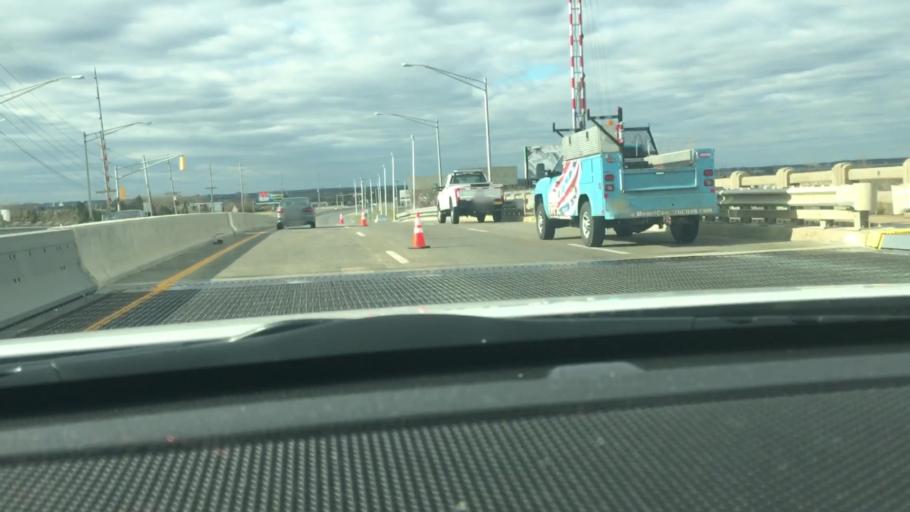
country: US
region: New Jersey
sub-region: Atlantic County
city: Atlantic City
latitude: 39.3775
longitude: -74.4526
